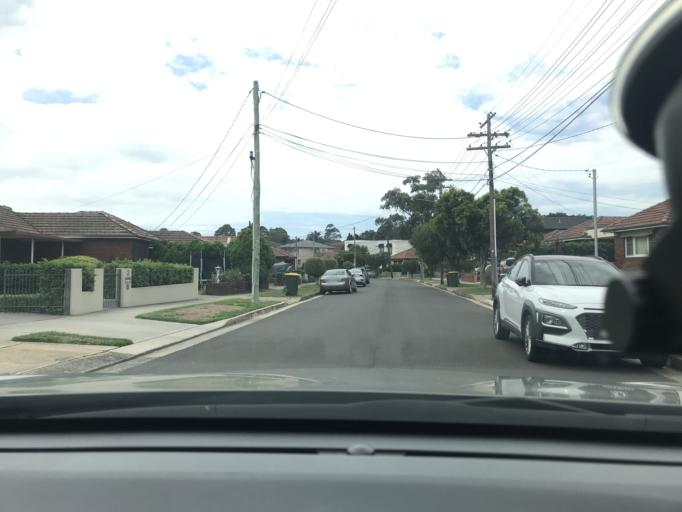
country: AU
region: New South Wales
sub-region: Canada Bay
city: Wareemba
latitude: -33.8634
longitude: 151.1273
